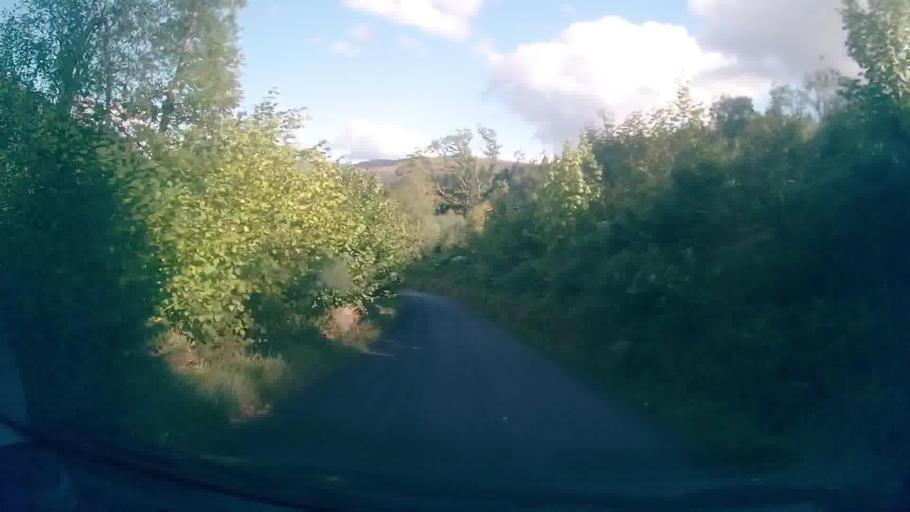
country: GB
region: Wales
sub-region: Merthyr Tydfil County Borough
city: Merthyr Tydfil
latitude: 51.8439
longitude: -3.3665
